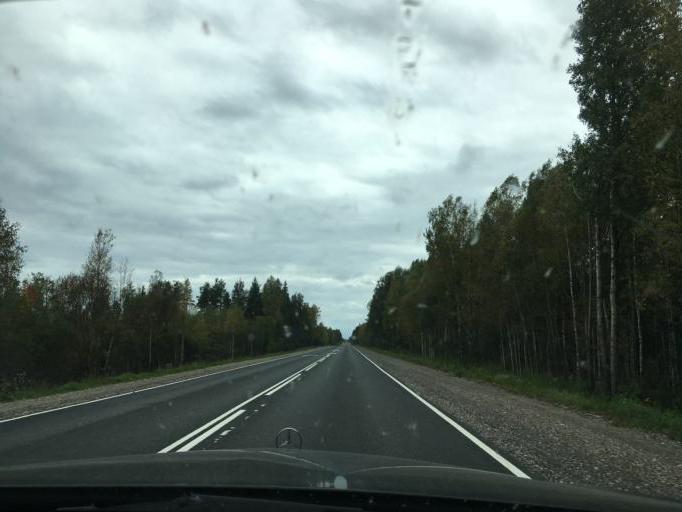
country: RU
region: Pskov
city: Pechory
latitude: 57.6699
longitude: 27.5246
